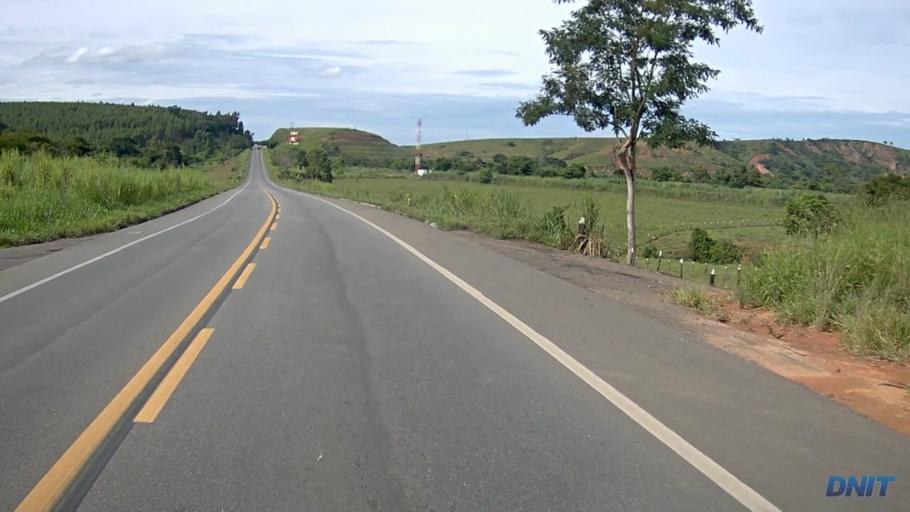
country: BR
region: Minas Gerais
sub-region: Belo Oriente
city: Belo Oriente
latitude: -19.2598
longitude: -42.3429
